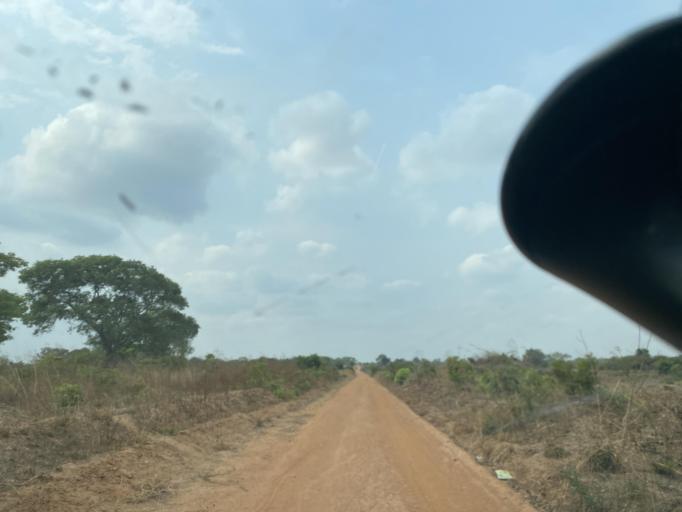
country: ZM
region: Lusaka
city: Lusaka
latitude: -15.1437
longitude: 28.3664
